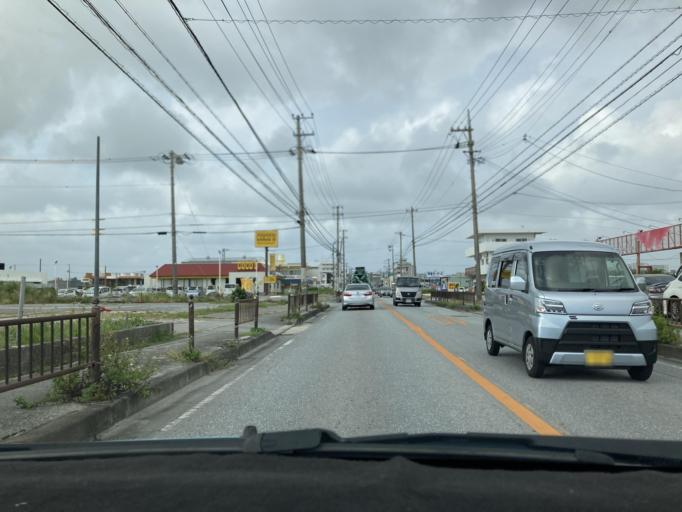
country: JP
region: Okinawa
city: Tomigusuku
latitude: 26.1670
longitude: 127.6680
